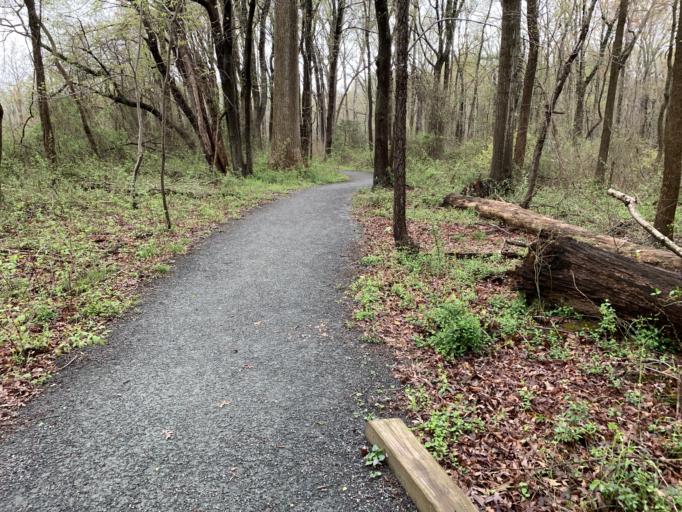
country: US
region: Delaware
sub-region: Kent County
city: Cheswold
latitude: 39.1813
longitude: -75.5811
